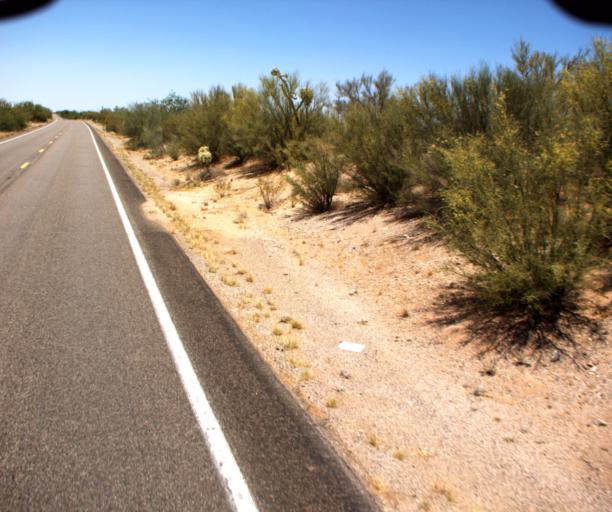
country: US
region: Arizona
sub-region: Pima County
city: Catalina
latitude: 32.7192
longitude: -111.1064
